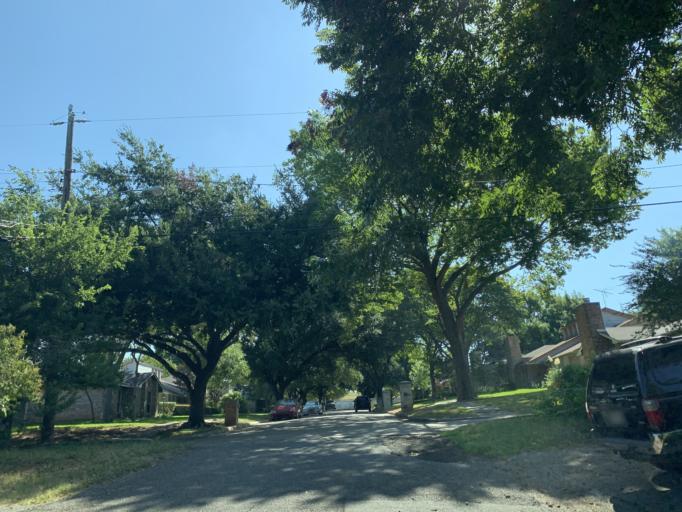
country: US
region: Texas
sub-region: Dallas County
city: Cockrell Hill
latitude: 32.7431
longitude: -96.8652
